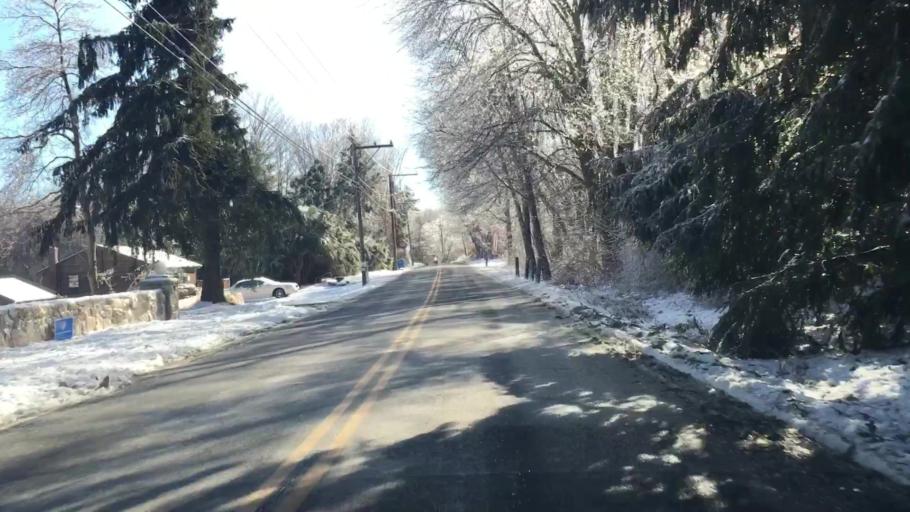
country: US
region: Connecticut
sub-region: Fairfield County
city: Newtown
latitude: 41.3611
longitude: -73.2397
